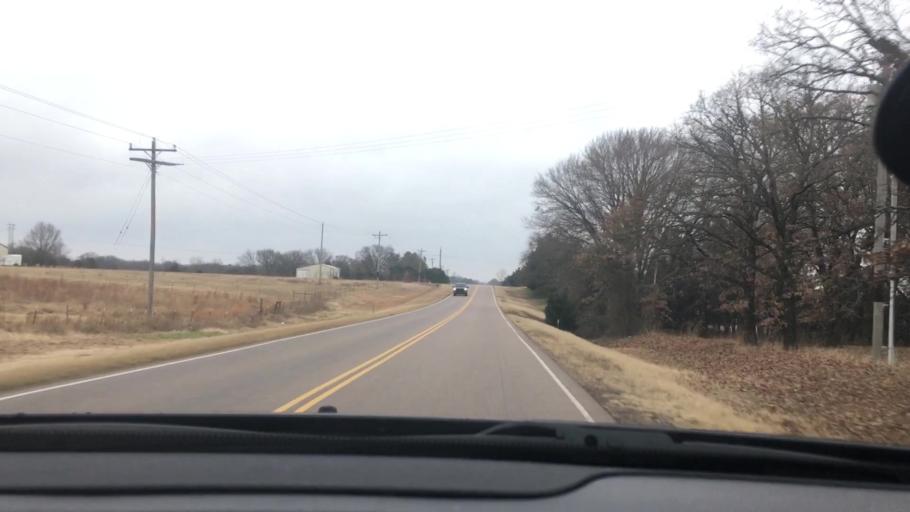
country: US
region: Oklahoma
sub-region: Johnston County
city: Tishomingo
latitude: 34.2730
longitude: -96.6711
